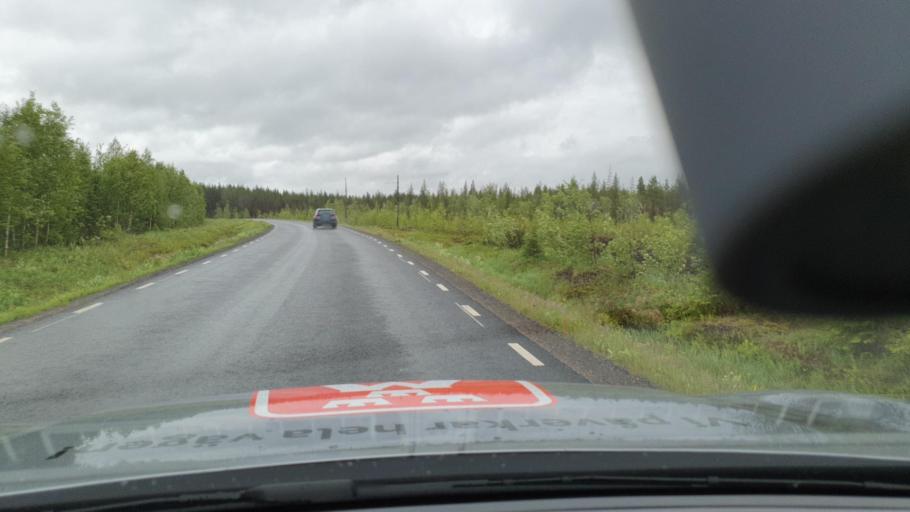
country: FI
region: Lapland
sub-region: Torniolaakso
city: Ylitornio
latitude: 66.1657
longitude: 23.8308
